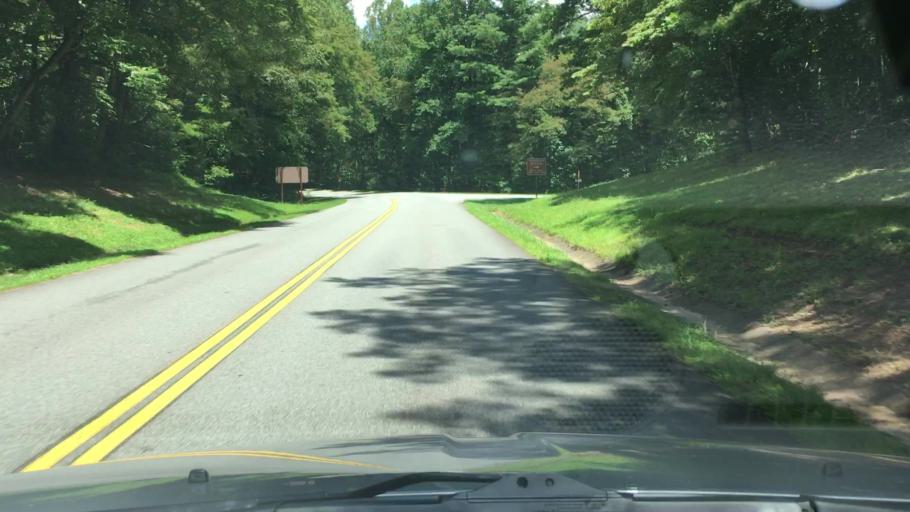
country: US
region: North Carolina
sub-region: Buncombe County
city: Biltmore Forest
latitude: 35.5896
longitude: -82.4788
